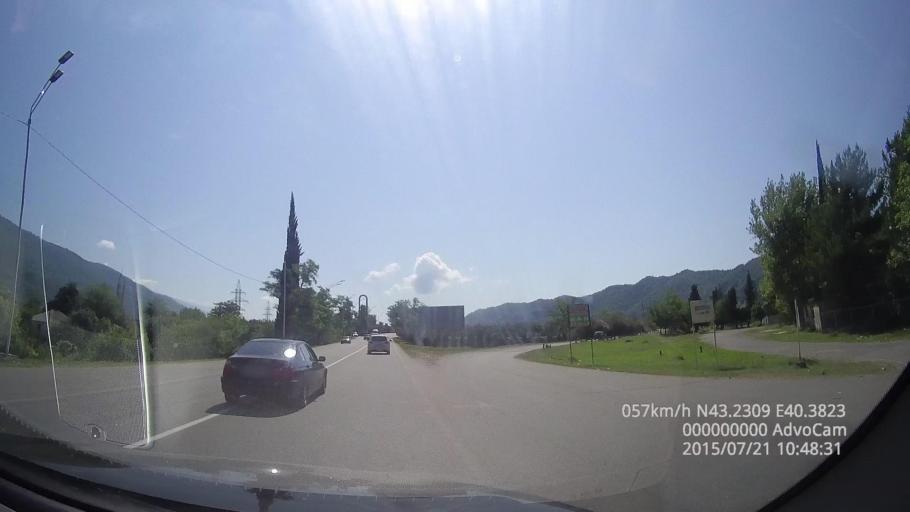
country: GE
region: Abkhazia
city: Bich'vinta
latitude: 43.2308
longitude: 40.3749
